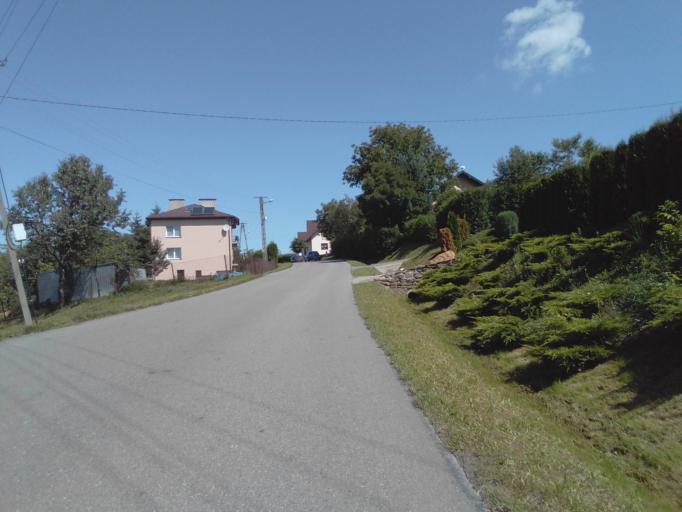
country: PL
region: Subcarpathian Voivodeship
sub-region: Powiat krosnienski
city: Chorkowka
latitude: 49.6523
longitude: 21.6078
